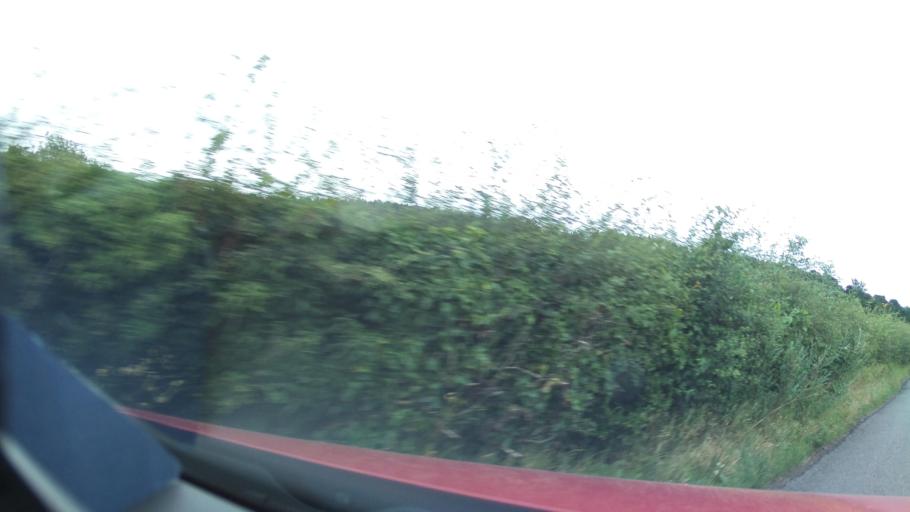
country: GB
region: England
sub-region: Derbyshire
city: Repton
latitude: 52.8103
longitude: -1.5438
